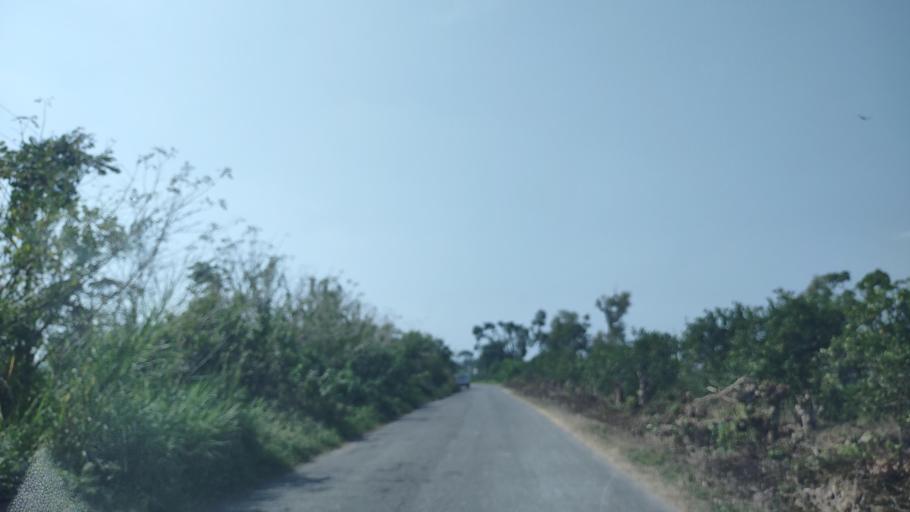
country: MX
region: Puebla
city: Espinal
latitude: 20.2584
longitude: -97.3202
